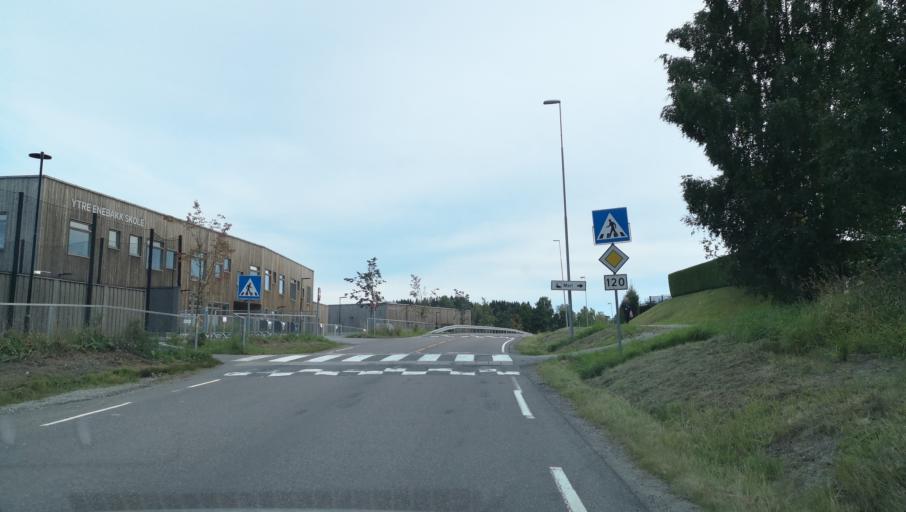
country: NO
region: Ostfold
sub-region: Hobol
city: Tomter
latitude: 59.7218
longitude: 11.0552
